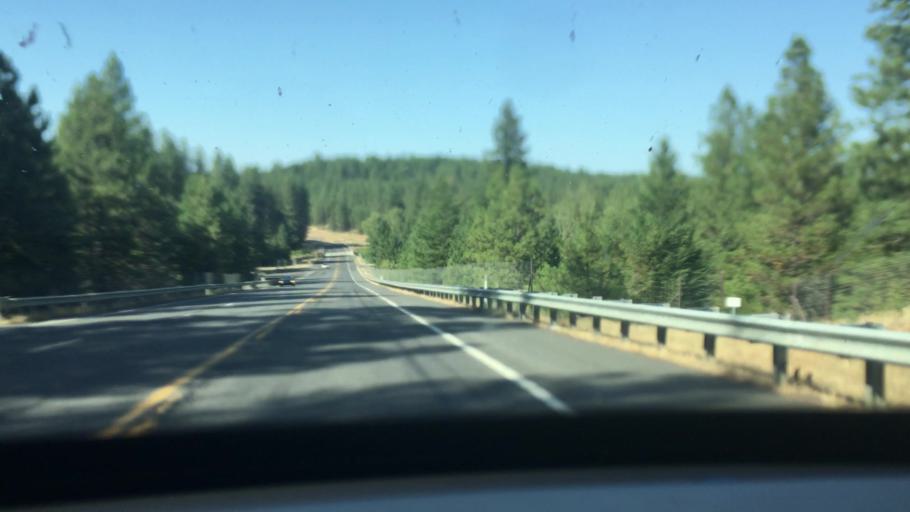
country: US
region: Washington
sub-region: Klickitat County
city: Goldendale
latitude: 45.9111
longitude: -120.7088
